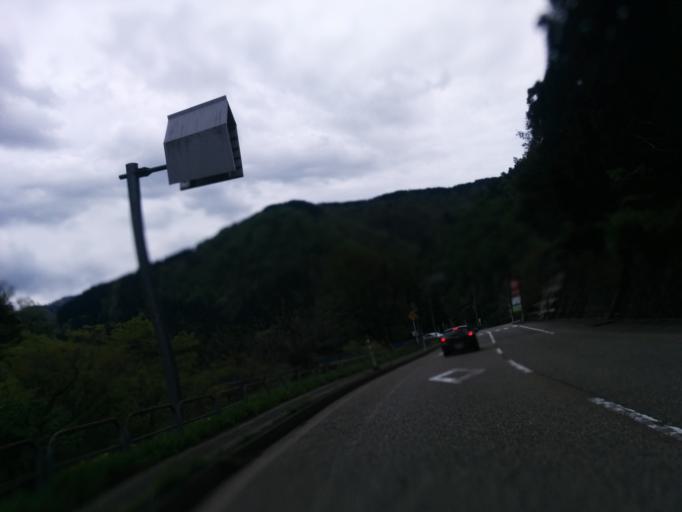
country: JP
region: Toyama
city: Fukumitsu
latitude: 36.4013
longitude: 136.9163
